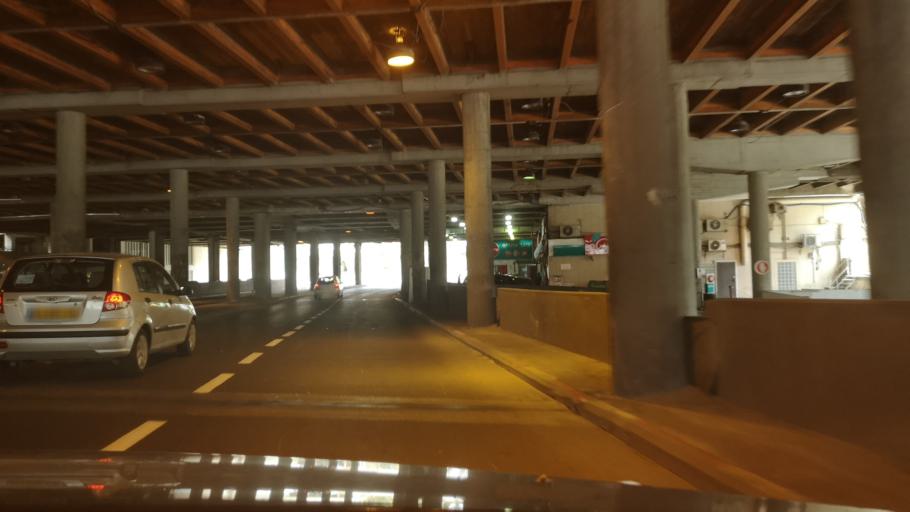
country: IL
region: Tel Aviv
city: Tel Aviv
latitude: 32.0854
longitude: 34.7698
